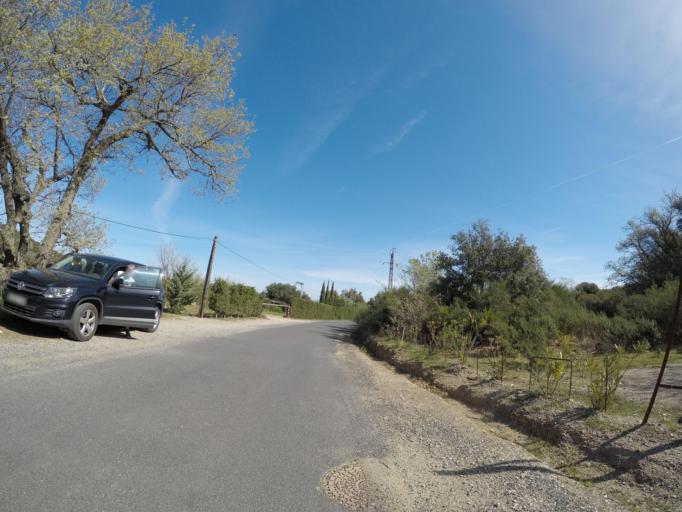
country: FR
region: Languedoc-Roussillon
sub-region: Departement des Pyrenees-Orientales
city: Millas
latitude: 42.6407
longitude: 2.7008
